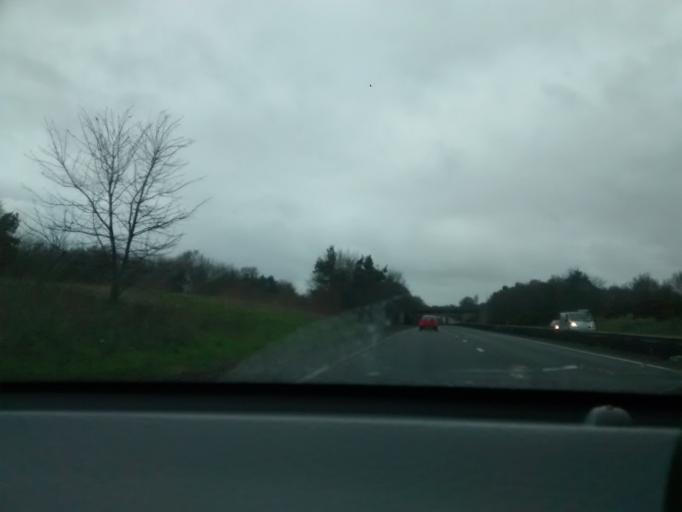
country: GB
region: England
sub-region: Suffolk
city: Felixstowe
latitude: 51.9870
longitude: 1.3207
